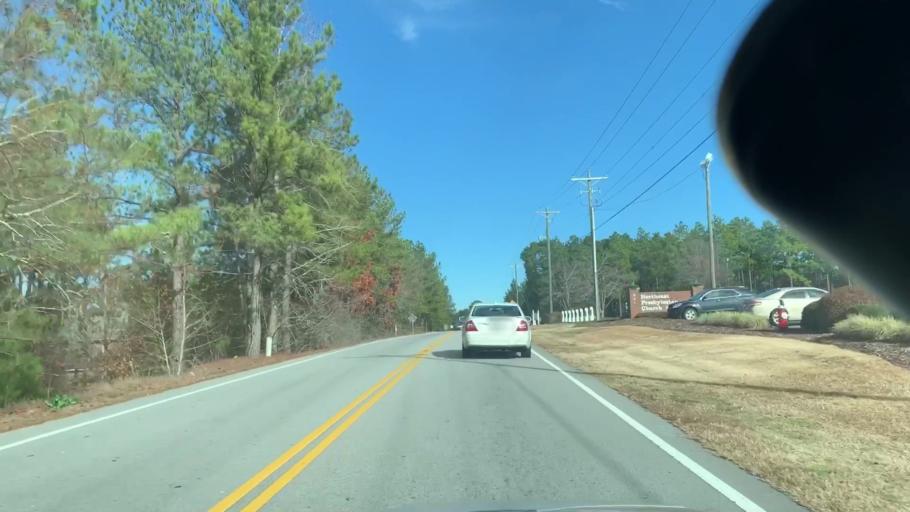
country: US
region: South Carolina
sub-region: Richland County
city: Woodfield
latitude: 34.0959
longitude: -80.8928
